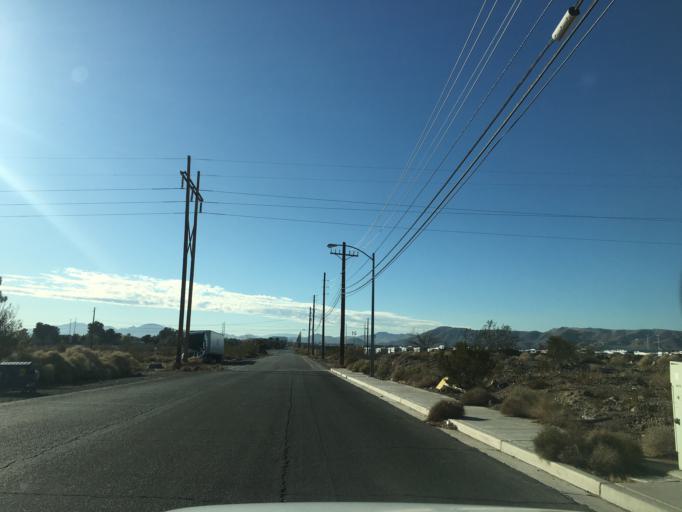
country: US
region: Nevada
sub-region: Clark County
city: Enterprise
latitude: 36.0106
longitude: -115.1702
